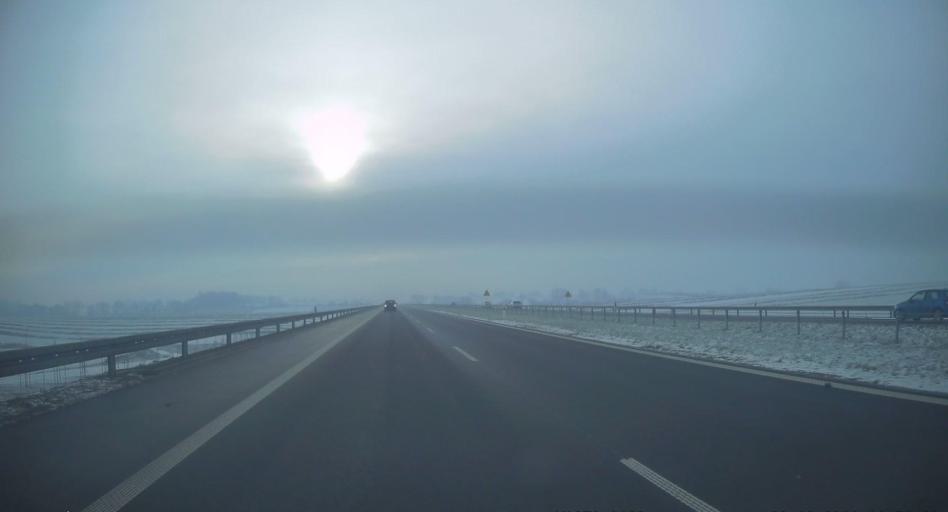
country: PL
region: Lesser Poland Voivodeship
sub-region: Powiat krakowski
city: Slomniki
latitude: 50.2817
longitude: 20.0225
